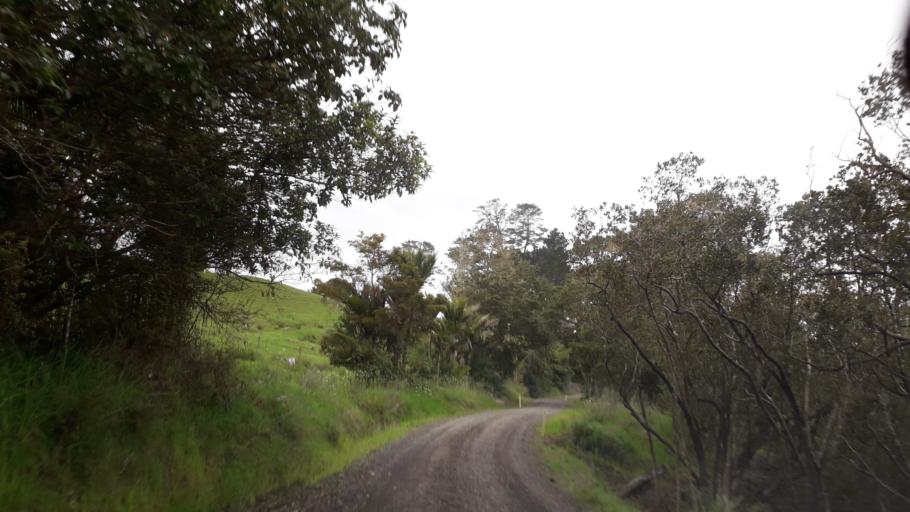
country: NZ
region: Northland
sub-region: Far North District
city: Waimate North
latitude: -35.3163
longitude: 173.5686
